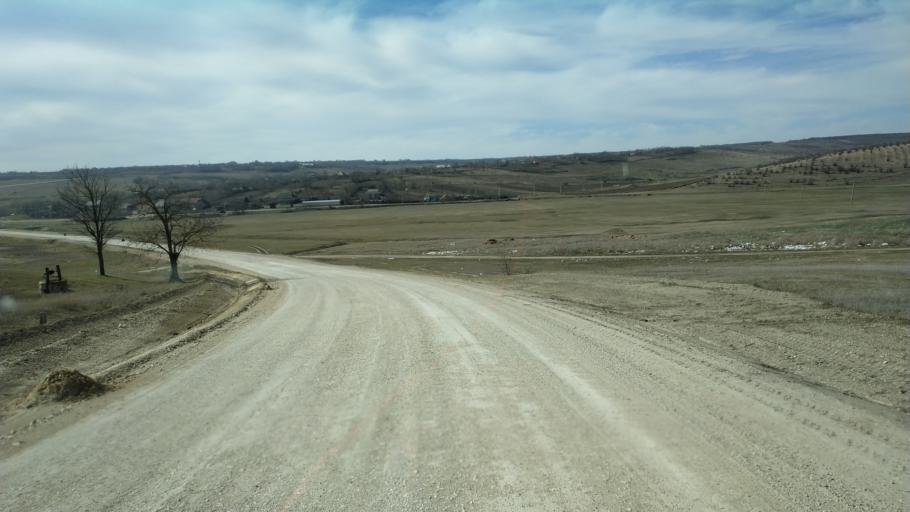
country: MD
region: Nisporeni
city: Nisporeni
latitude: 46.9744
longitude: 28.1873
